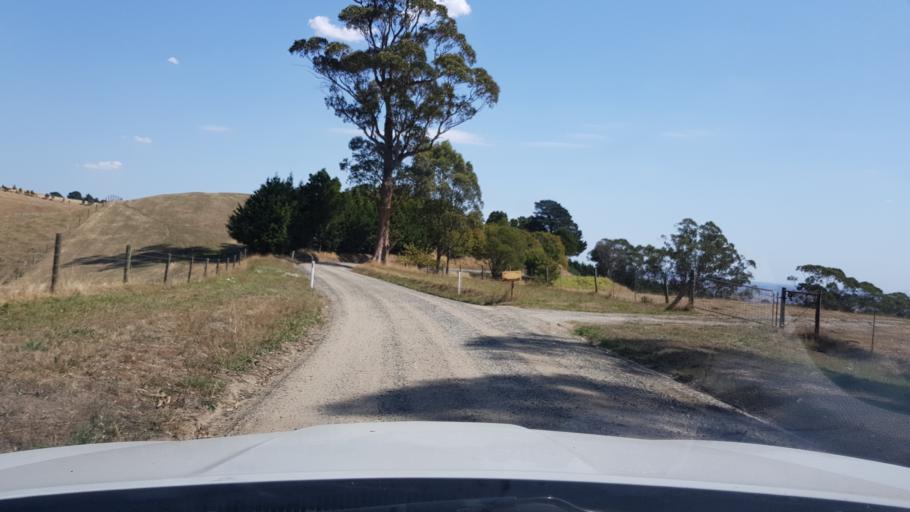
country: AU
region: Victoria
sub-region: Baw Baw
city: Warragul
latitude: -38.2856
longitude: 145.9208
